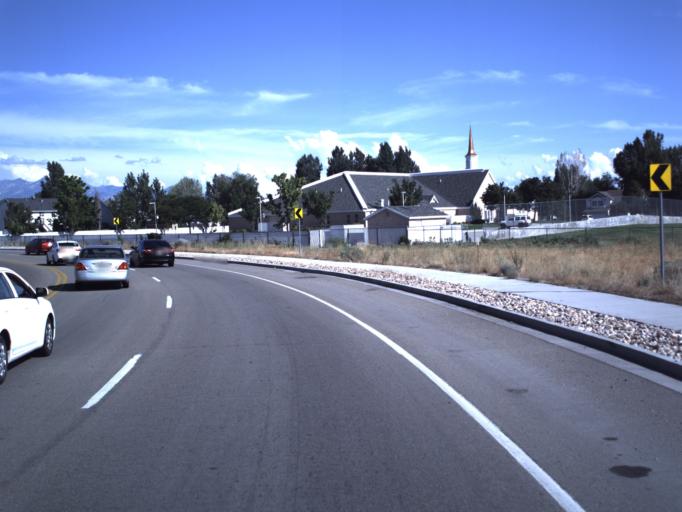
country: US
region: Utah
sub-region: Utah County
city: Lehi
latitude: 40.4123
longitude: -111.8724
